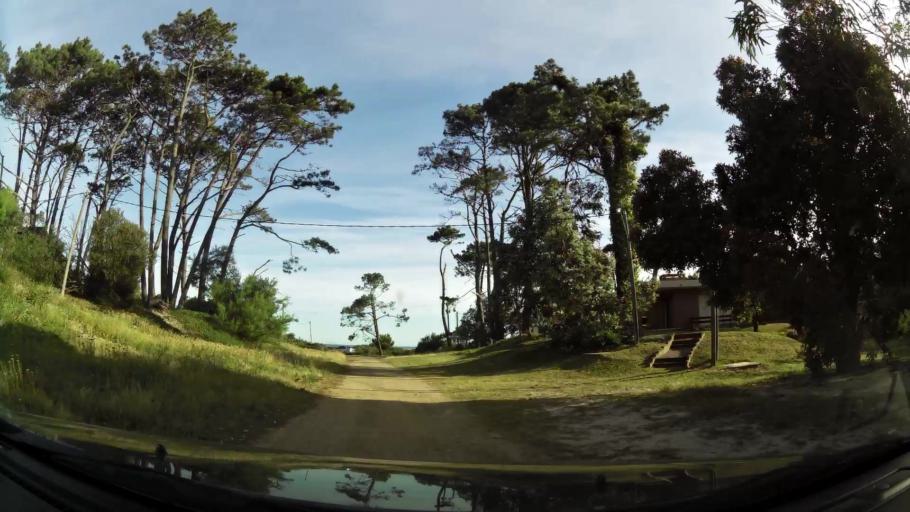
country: UY
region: Canelones
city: Atlantida
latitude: -34.7904
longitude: -55.8539
